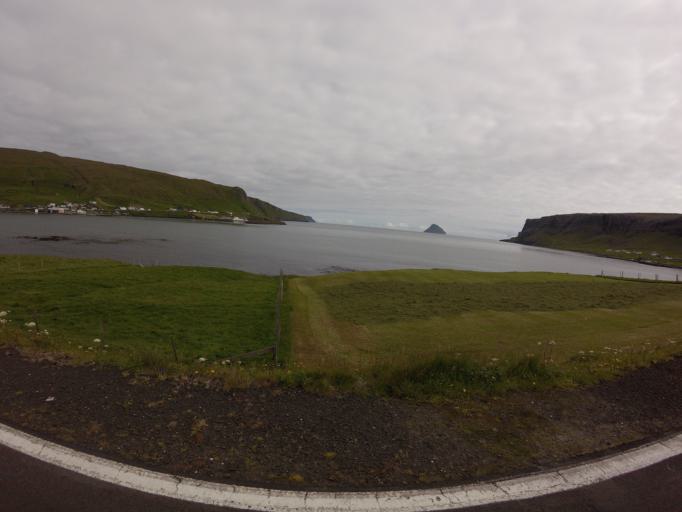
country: FO
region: Suduroy
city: Tvoroyri
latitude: 61.5969
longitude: -6.9470
